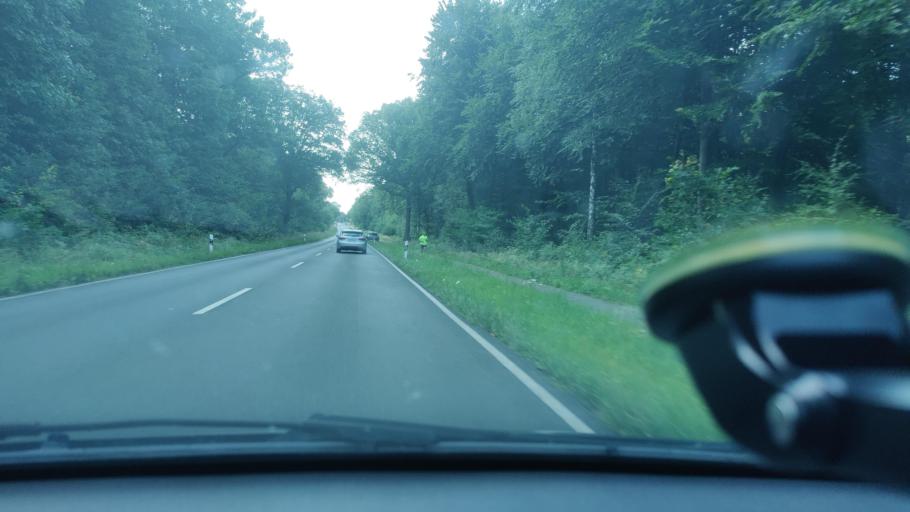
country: DE
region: North Rhine-Westphalia
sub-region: Regierungsbezirk Dusseldorf
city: Alpen
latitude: 51.5601
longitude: 6.4983
